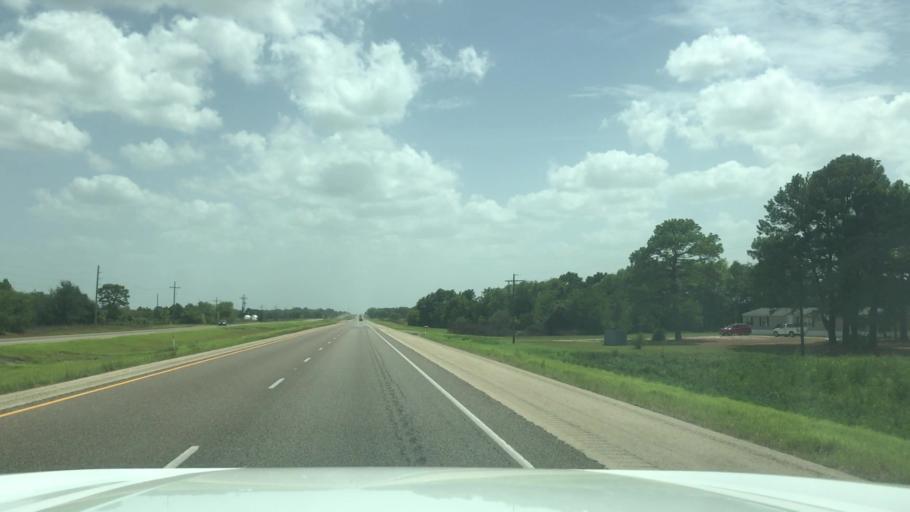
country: US
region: Texas
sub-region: Robertson County
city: Calvert
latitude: 31.0799
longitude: -96.7136
